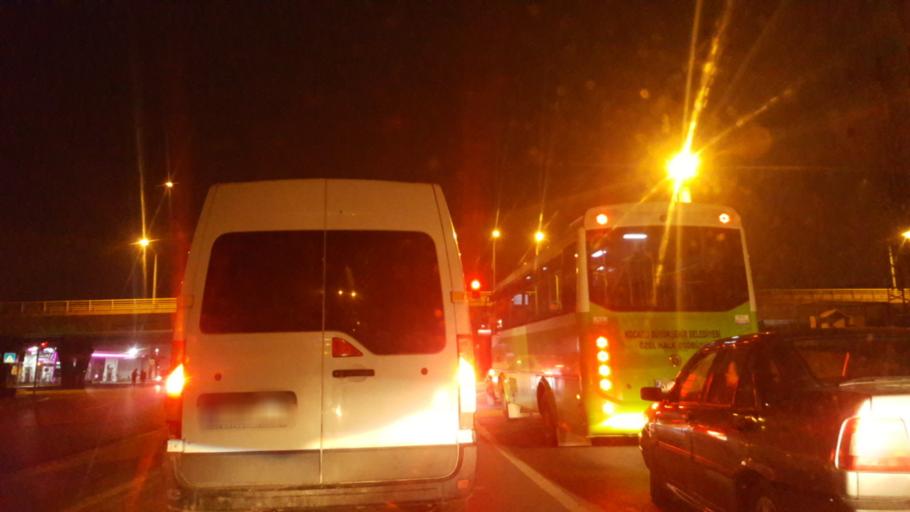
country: TR
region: Kocaeli
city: Darica
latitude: 40.7906
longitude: 29.4023
